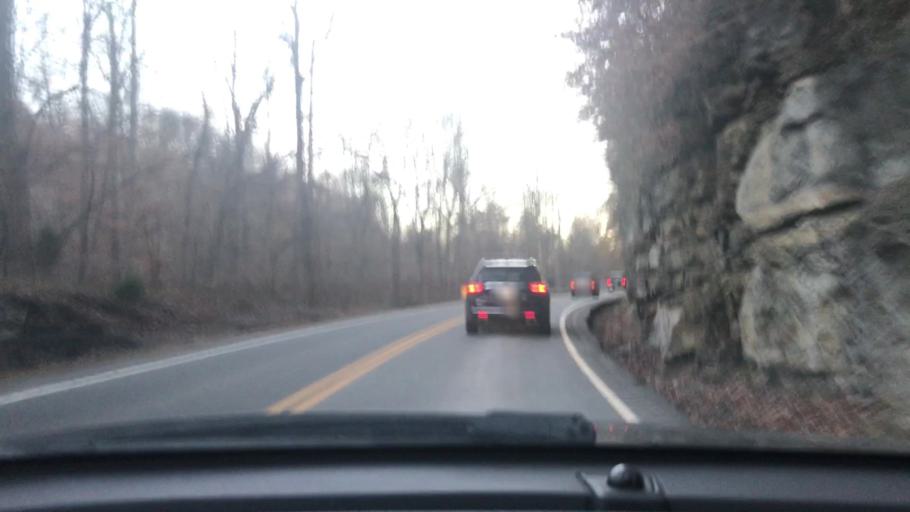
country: US
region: Tennessee
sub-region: Cheatham County
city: Ashland City
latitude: 36.3069
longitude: -87.0445
